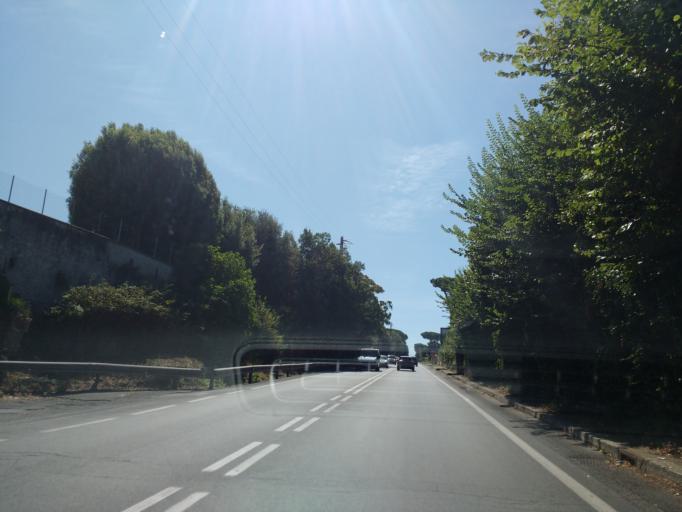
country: IT
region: Latium
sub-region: Citta metropolitana di Roma Capitale
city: Castel Gandolfo
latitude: 41.7492
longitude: 12.6359
